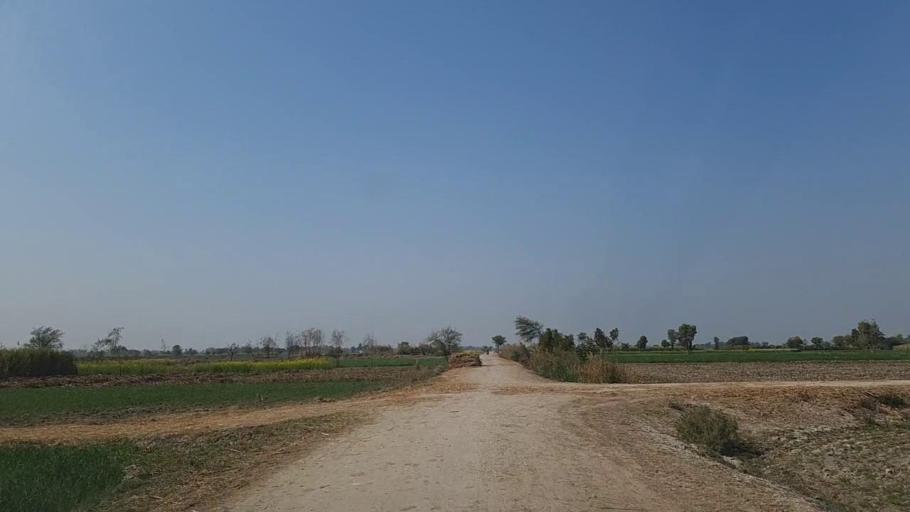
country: PK
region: Sindh
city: Daur
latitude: 26.4412
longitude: 68.2982
